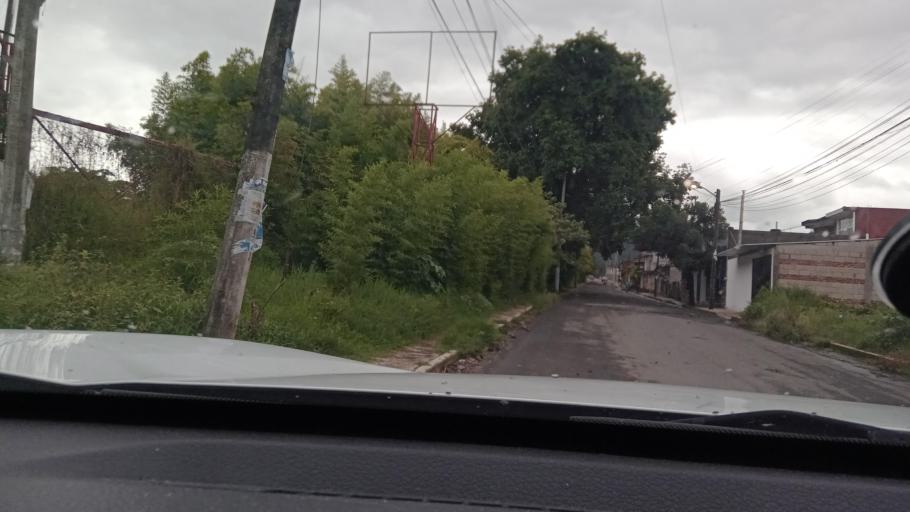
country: MX
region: Veracruz
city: Coatepec
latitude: 19.4508
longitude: -96.9739
